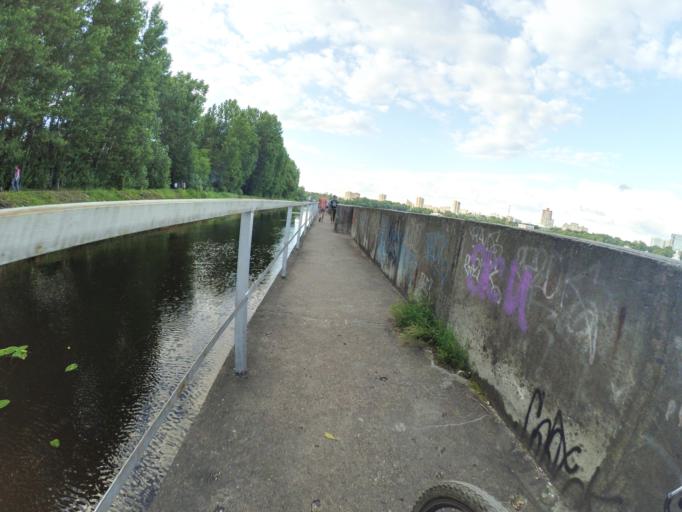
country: RU
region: Moskovskaya
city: Levoberezhnyy
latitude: 55.8386
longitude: 37.4662
